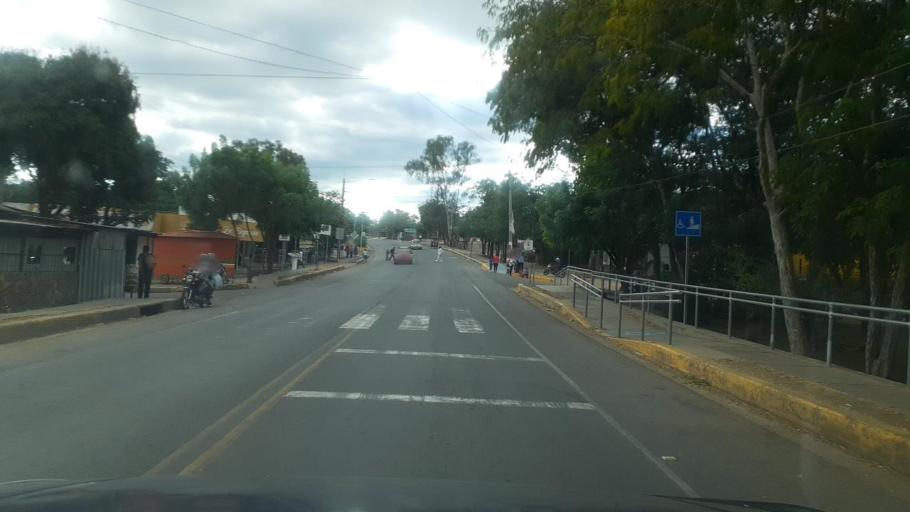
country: NI
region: Madriz
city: Somoto
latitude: 13.4883
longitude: -86.5812
